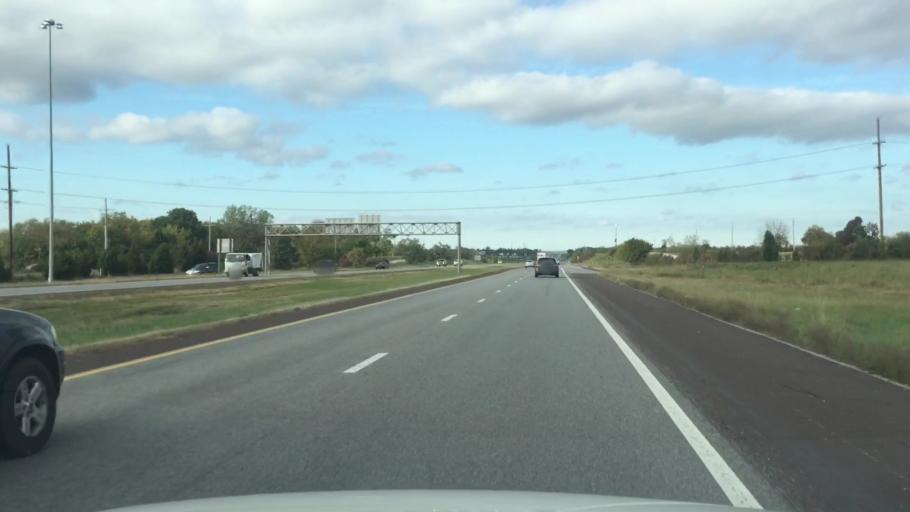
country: US
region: Kansas
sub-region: Johnson County
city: Olathe
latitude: 38.9438
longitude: -94.8527
